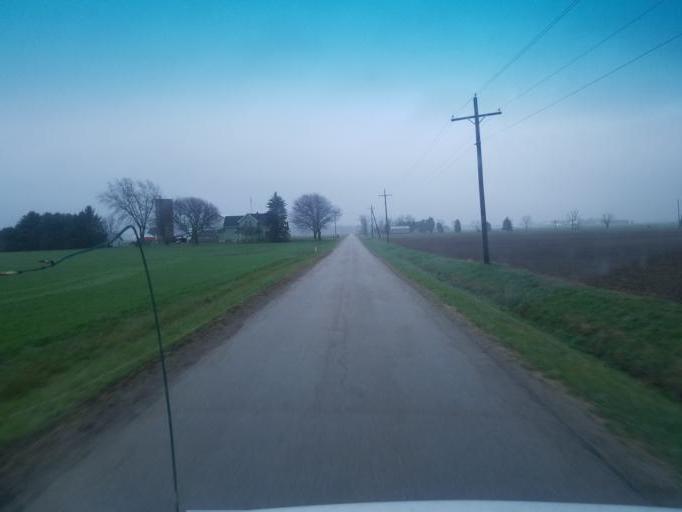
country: US
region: Ohio
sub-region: Fulton County
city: Archbold
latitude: 41.4202
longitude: -84.2477
